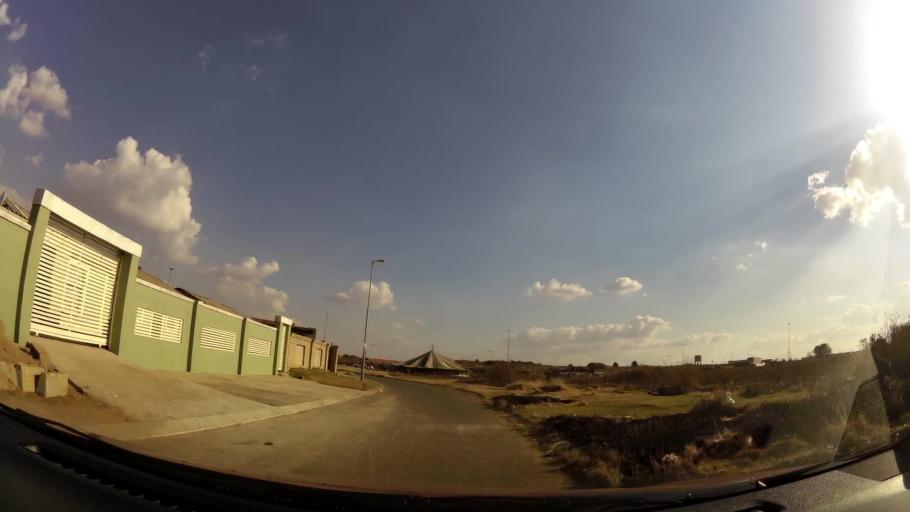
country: ZA
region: Gauteng
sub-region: City of Johannesburg Metropolitan Municipality
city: Soweto
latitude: -26.2306
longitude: 27.8665
